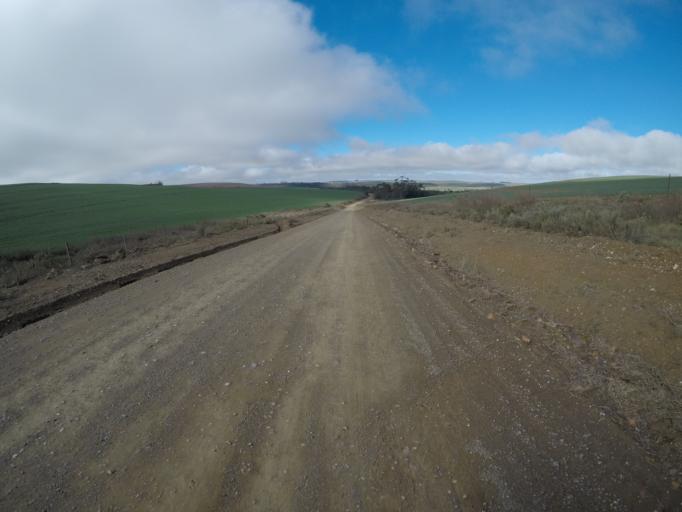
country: ZA
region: Western Cape
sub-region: Overberg District Municipality
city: Caledon
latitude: -34.1101
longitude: 19.7679
